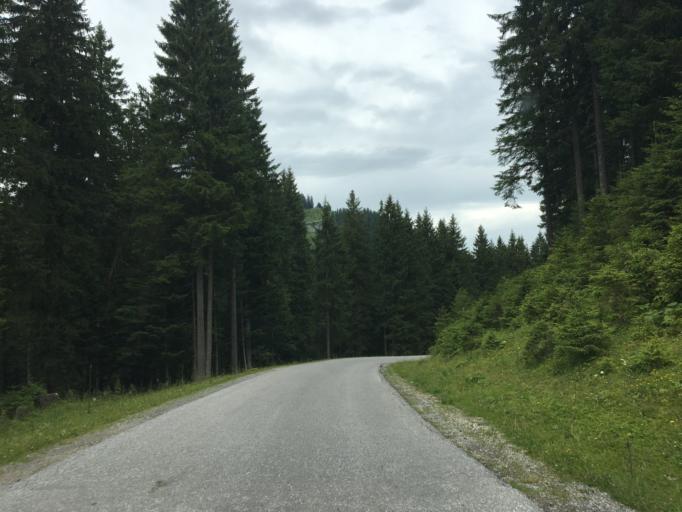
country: AT
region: Salzburg
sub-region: Politischer Bezirk Hallein
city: Abtenau
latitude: 47.6325
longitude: 13.4133
